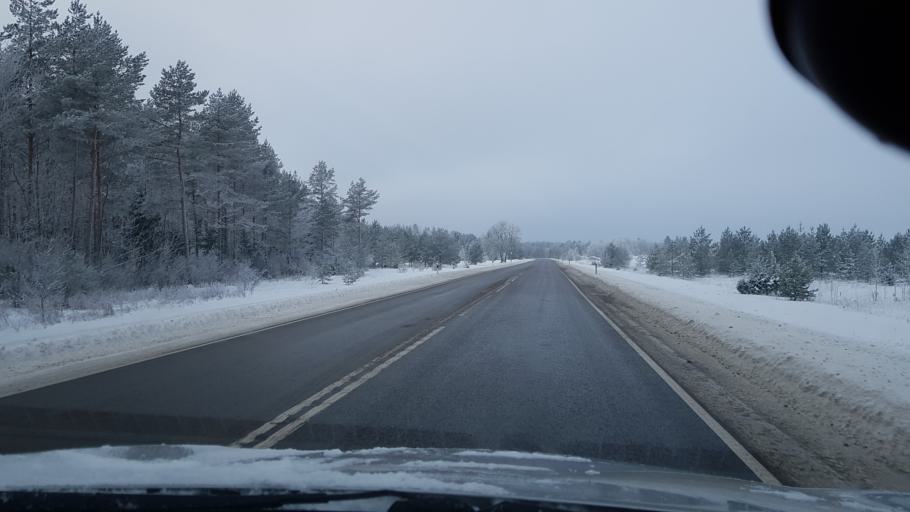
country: EE
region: Harju
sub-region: Keila linn
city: Keila
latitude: 59.3274
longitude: 24.3655
